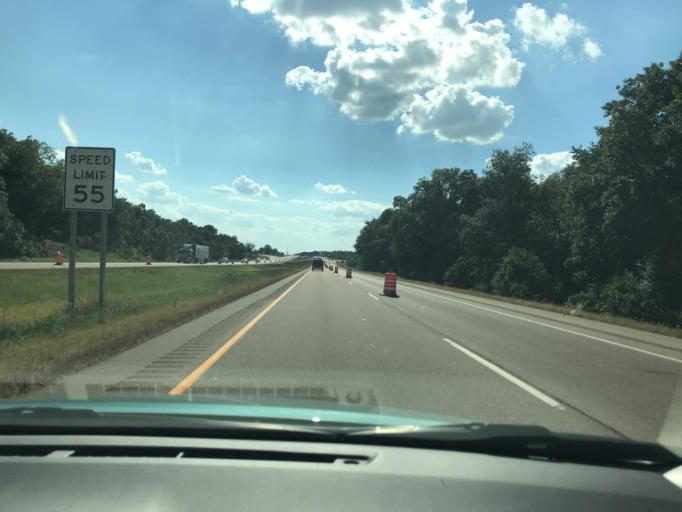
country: US
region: Wisconsin
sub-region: Rock County
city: Clinton
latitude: 42.5457
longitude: -88.9399
